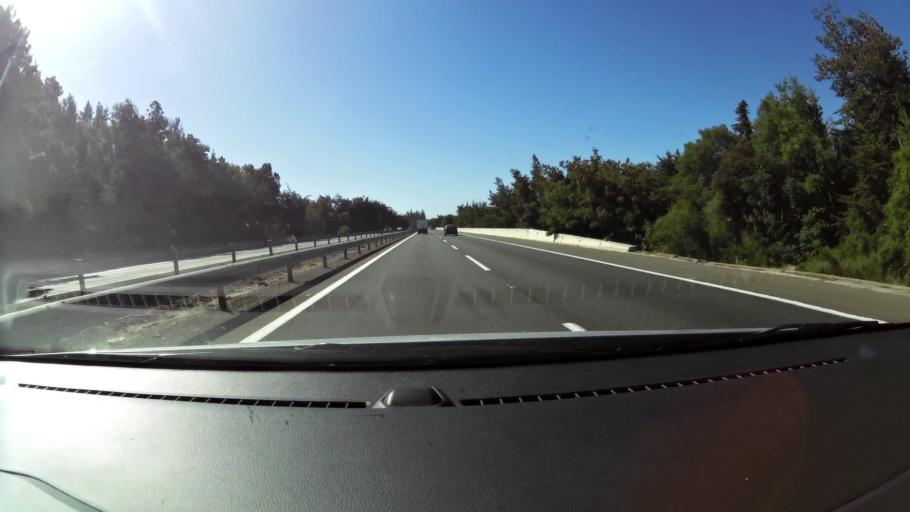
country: CL
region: Valparaiso
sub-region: Provincia de Marga Marga
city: Quilpue
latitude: -33.1838
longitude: -71.5031
